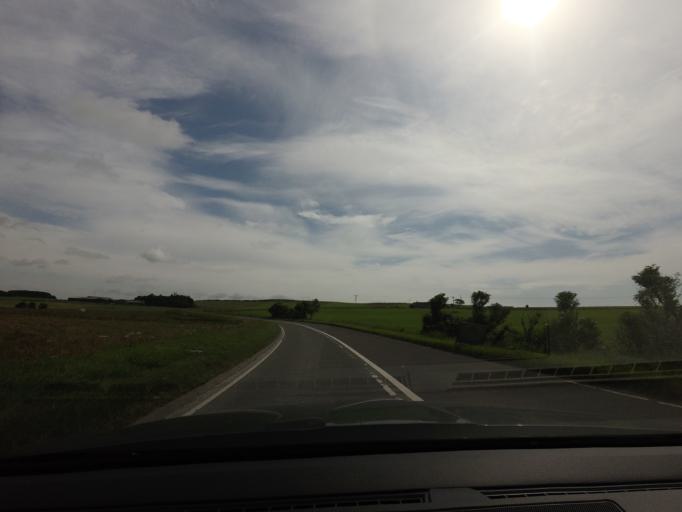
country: GB
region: Scotland
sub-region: Aberdeenshire
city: Rosehearty
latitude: 57.6003
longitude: -2.2310
